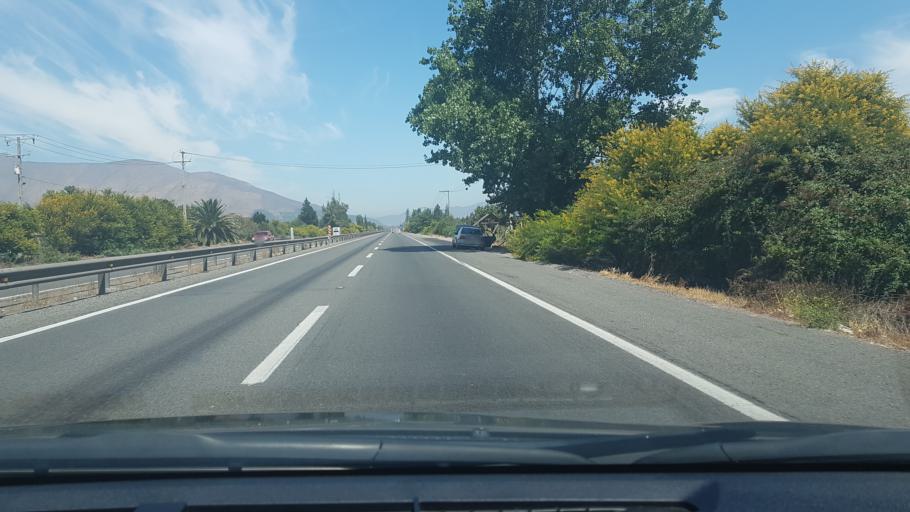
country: CL
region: Valparaiso
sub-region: Provincia de San Felipe
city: Llaillay
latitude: -32.8535
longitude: -70.9267
